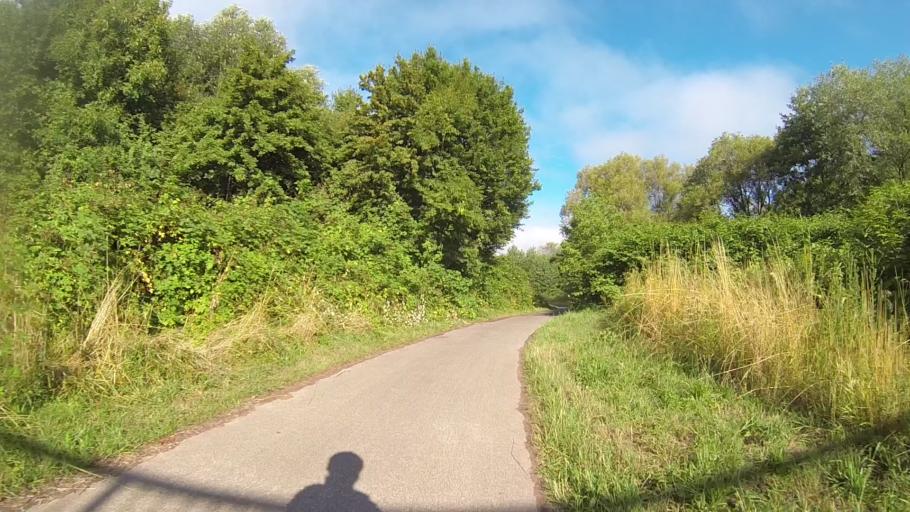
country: DE
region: Rheinland-Pfalz
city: Kenn
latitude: 49.8057
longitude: 6.6898
